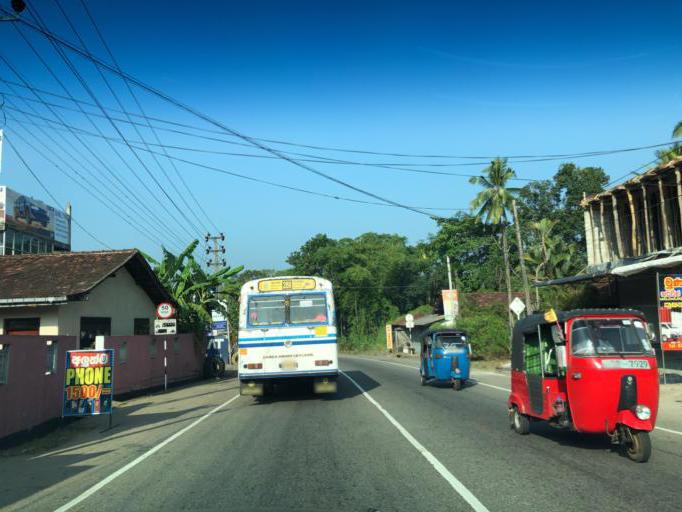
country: LK
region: Western
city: Horana South
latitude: 6.7236
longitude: 80.0828
